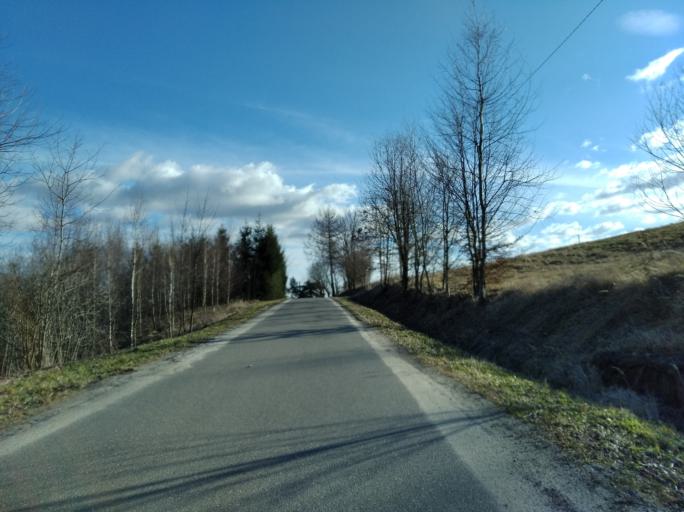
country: PL
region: Subcarpathian Voivodeship
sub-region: Powiat strzyzowski
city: Wisniowa
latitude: 49.8986
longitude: 21.7033
